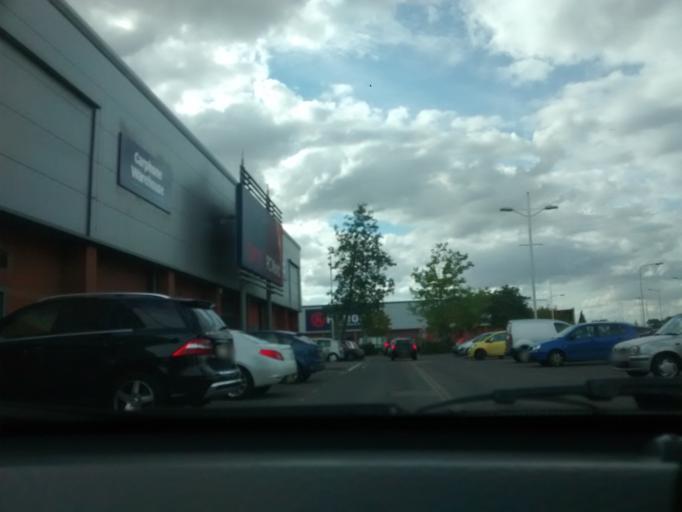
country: GB
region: England
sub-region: Norfolk
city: King's Lynn
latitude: 52.7373
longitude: 0.4139
